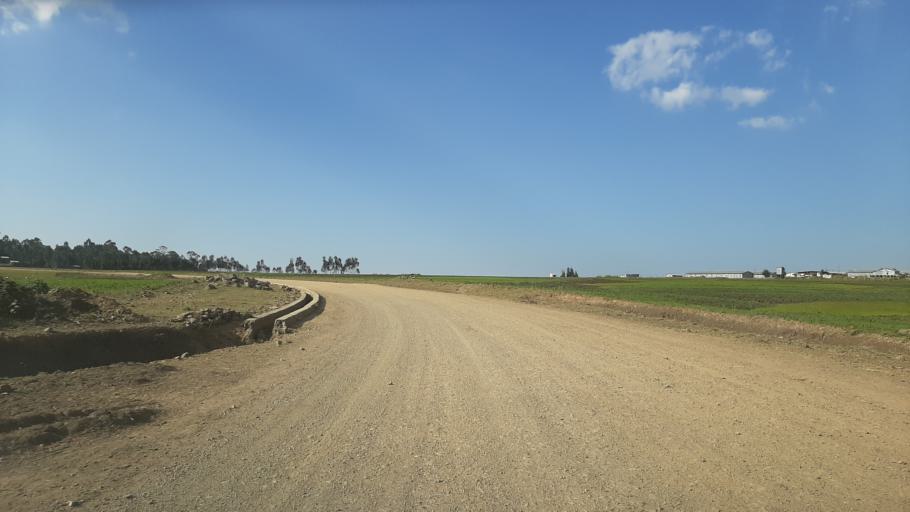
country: ET
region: Amhara
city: Dabat
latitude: 13.0102
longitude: 37.7617
